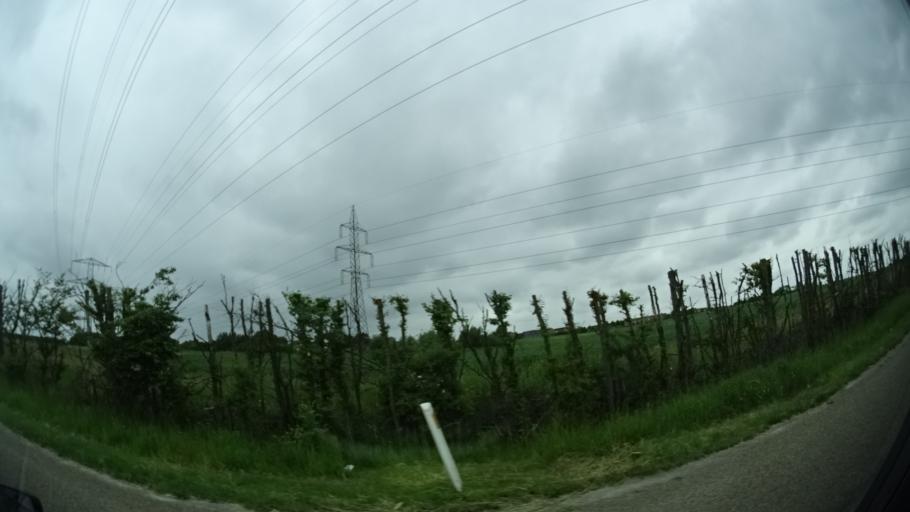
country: DK
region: Central Jutland
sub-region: Arhus Kommune
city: Logten
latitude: 56.2530
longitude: 10.3097
